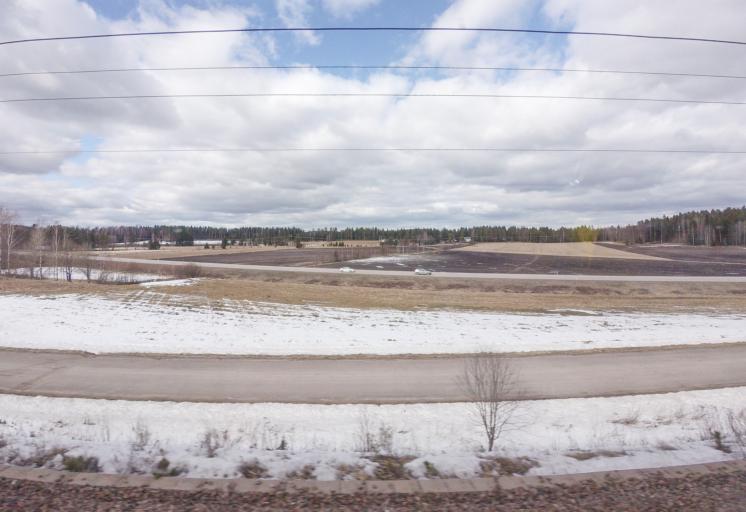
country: FI
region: Kymenlaakso
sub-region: Kotka-Hamina
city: Hamina
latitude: 60.9020
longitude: 27.1452
